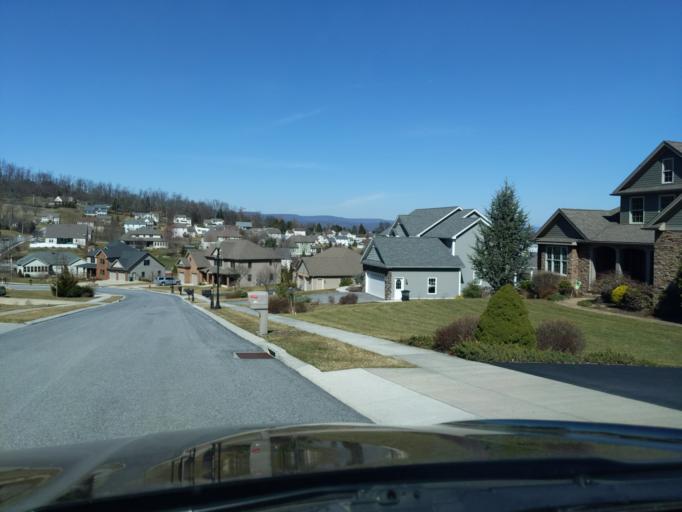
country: US
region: Pennsylvania
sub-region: Blair County
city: Duncansville
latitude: 40.4089
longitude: -78.4197
